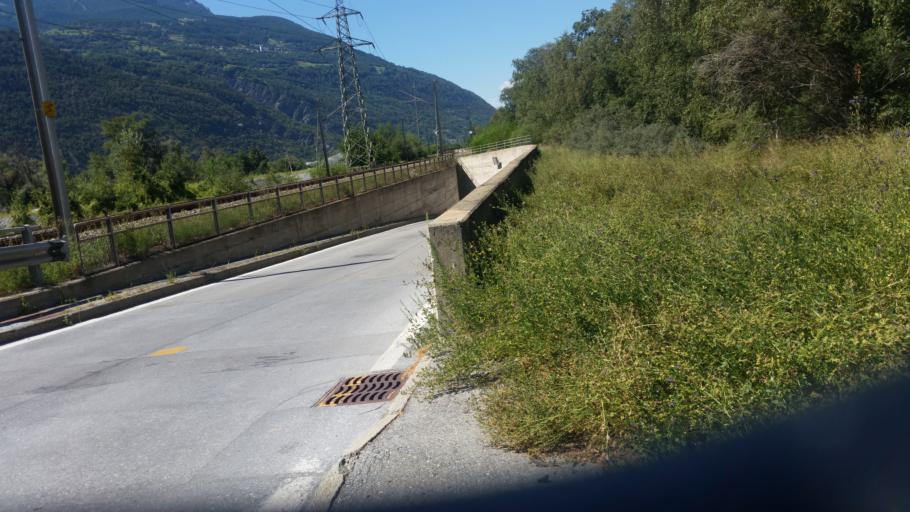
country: CH
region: Valais
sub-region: Raron District
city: Raron
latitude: 46.3081
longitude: 7.8272
